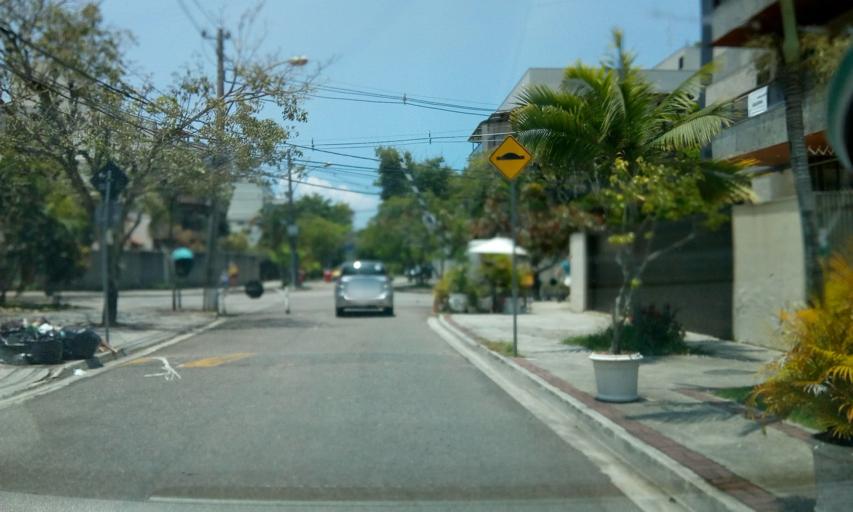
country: BR
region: Rio de Janeiro
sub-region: Nilopolis
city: Nilopolis
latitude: -23.0201
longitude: -43.4694
